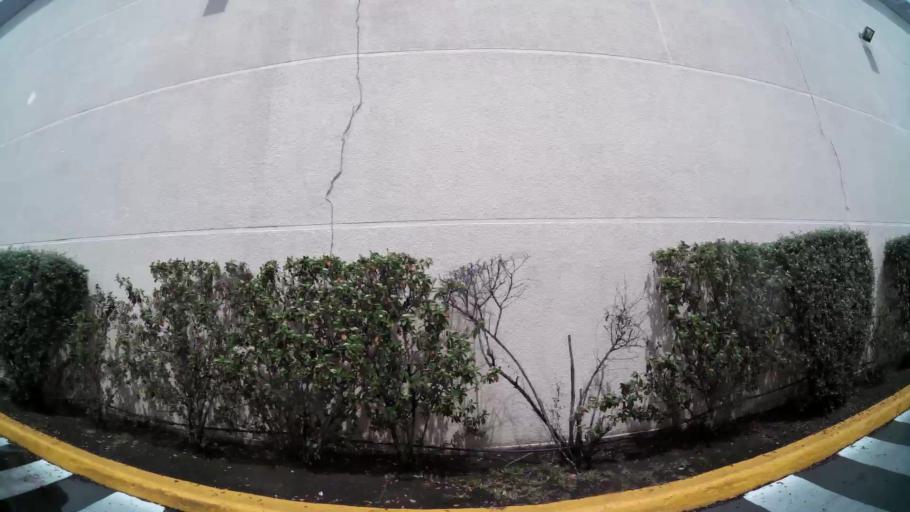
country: AR
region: Buenos Aires F.D.
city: Villa Lugano
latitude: -34.6753
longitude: -58.4593
